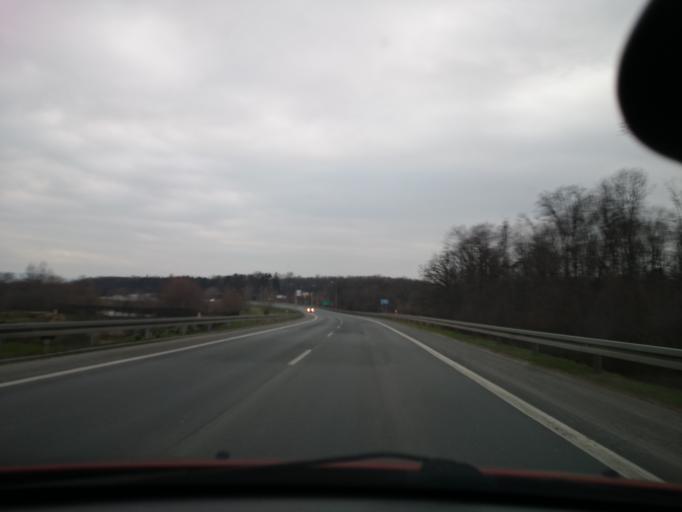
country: PL
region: Opole Voivodeship
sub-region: Powiat nyski
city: Otmuchow
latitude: 50.4580
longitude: 17.1736
